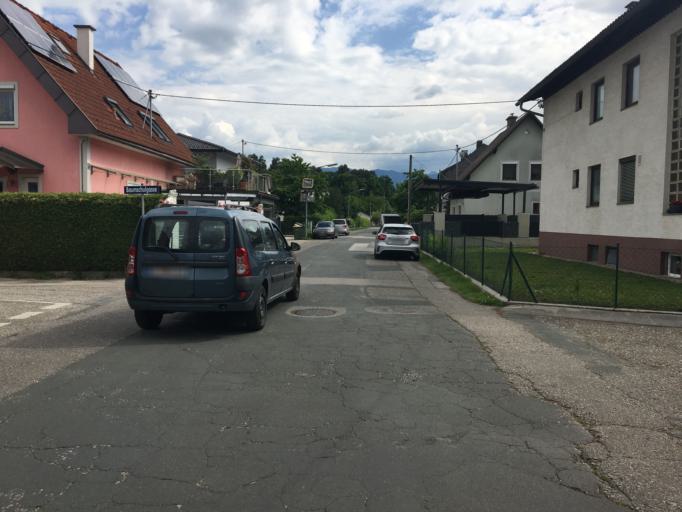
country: AT
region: Carinthia
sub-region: Klagenfurt am Woerthersee
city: Klagenfurt am Woerthersee
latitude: 46.6101
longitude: 14.2708
